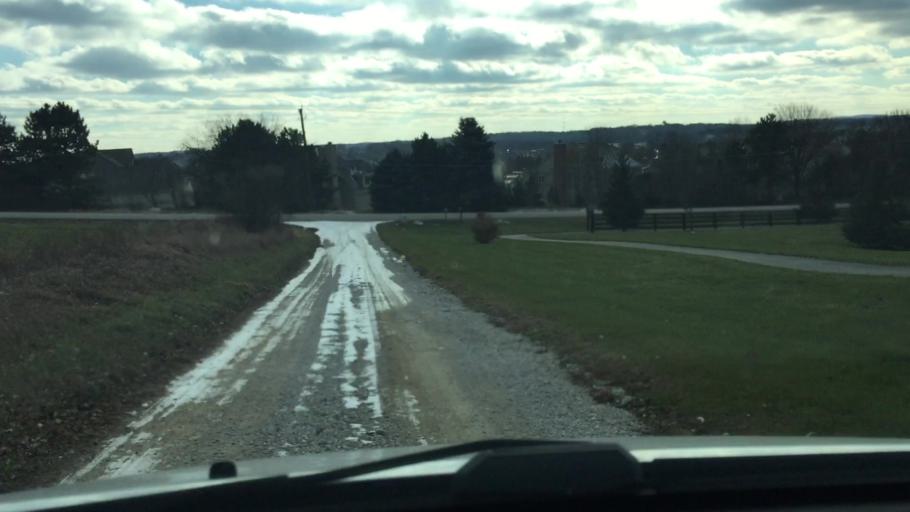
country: US
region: Wisconsin
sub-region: Waukesha County
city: Hartland
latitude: 43.1203
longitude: -88.3180
